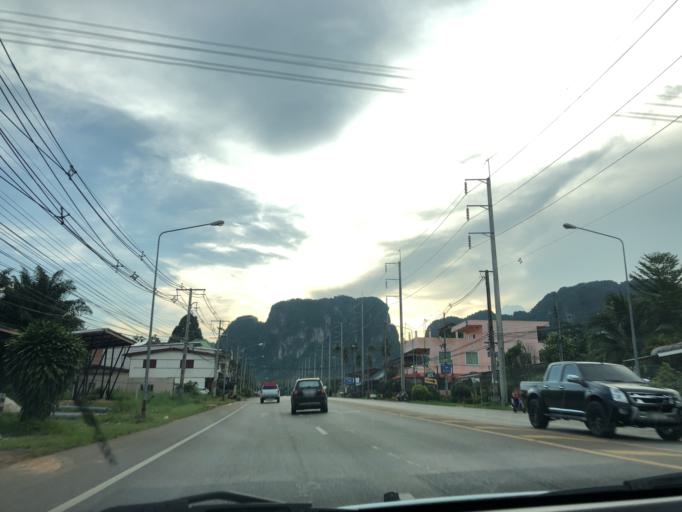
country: TH
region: Krabi
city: Krabi
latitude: 8.0831
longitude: 98.8661
